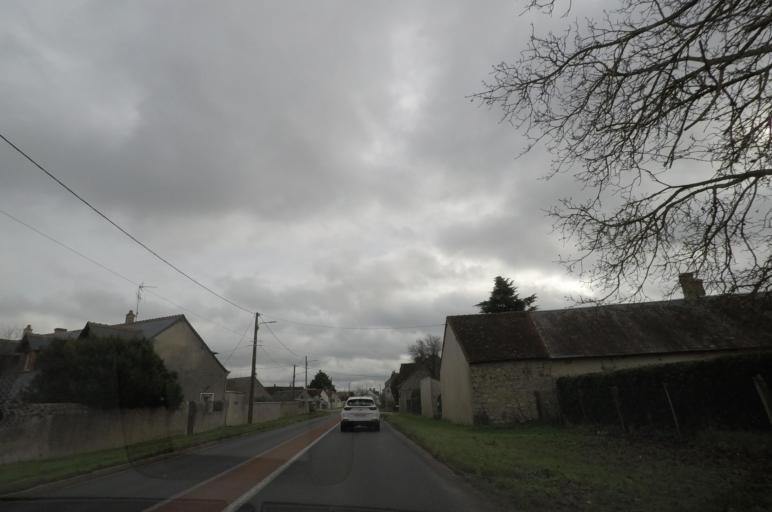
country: FR
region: Centre
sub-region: Departement du Loir-et-Cher
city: Herbault
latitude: 47.6887
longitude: 1.1945
